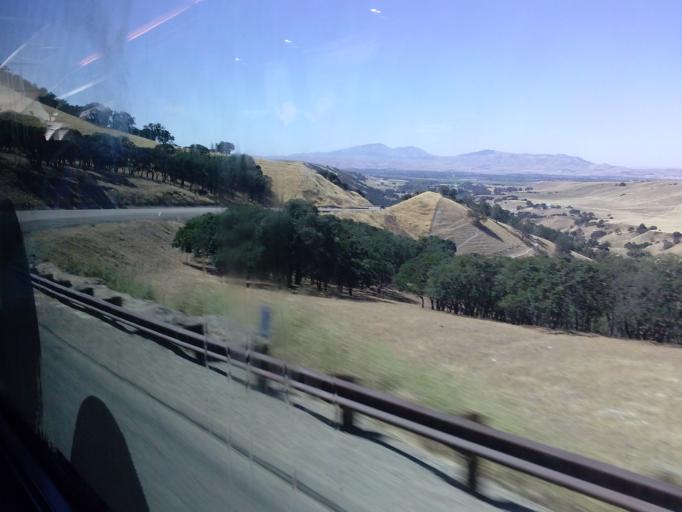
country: US
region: California
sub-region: Alameda County
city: Livermore
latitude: 37.6077
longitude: -121.6929
